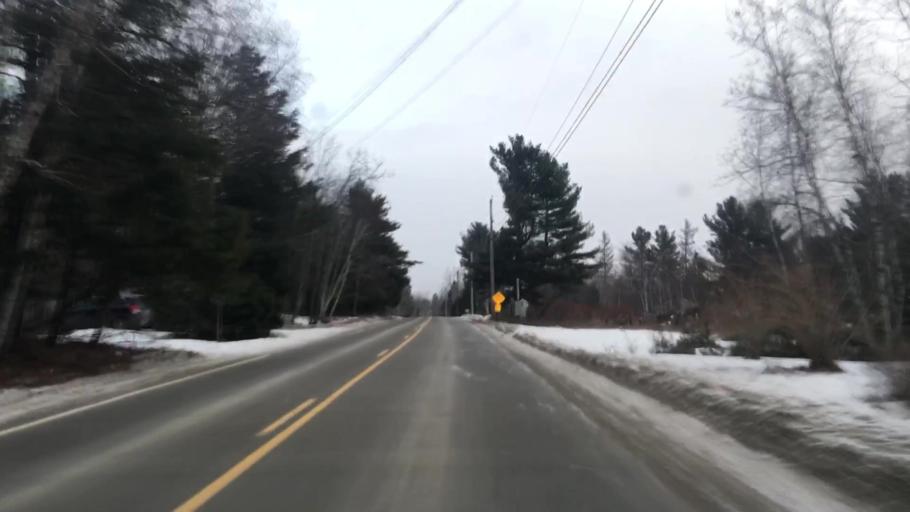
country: US
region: Maine
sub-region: Hancock County
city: Ellsworth
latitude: 44.6037
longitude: -68.3963
